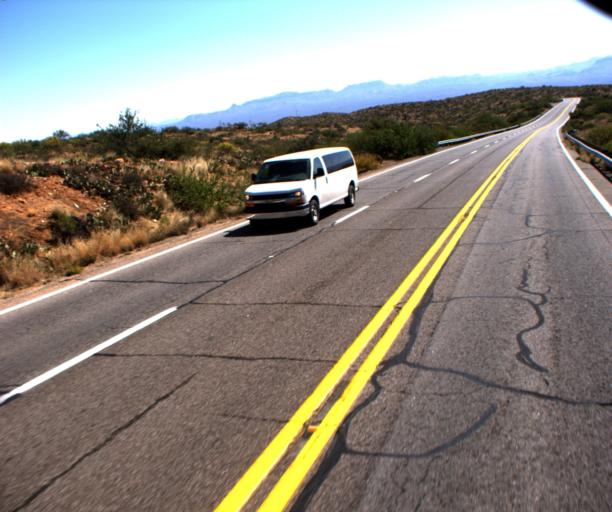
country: US
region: Arizona
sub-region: Pinal County
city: Oracle
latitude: 32.6501
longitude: -110.7101
